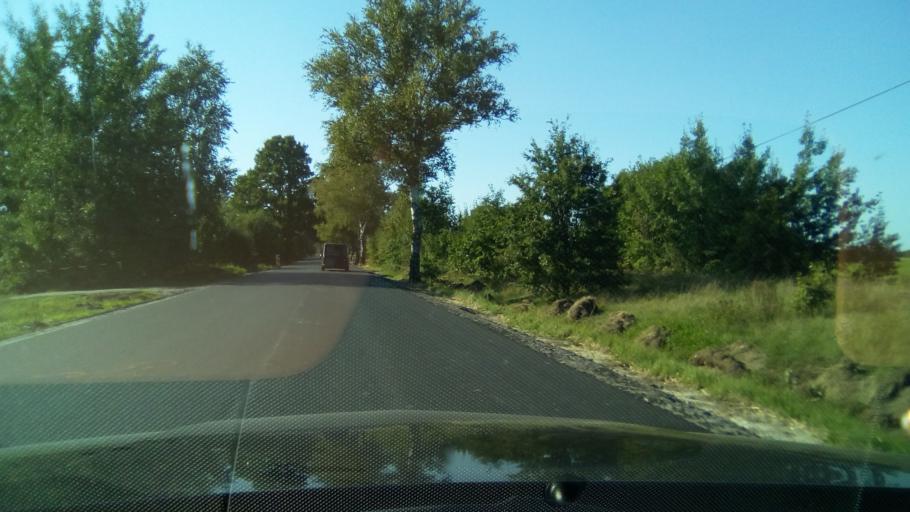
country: PL
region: West Pomeranian Voivodeship
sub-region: Powiat gryficki
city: Ploty
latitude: 53.8114
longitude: 15.1984
